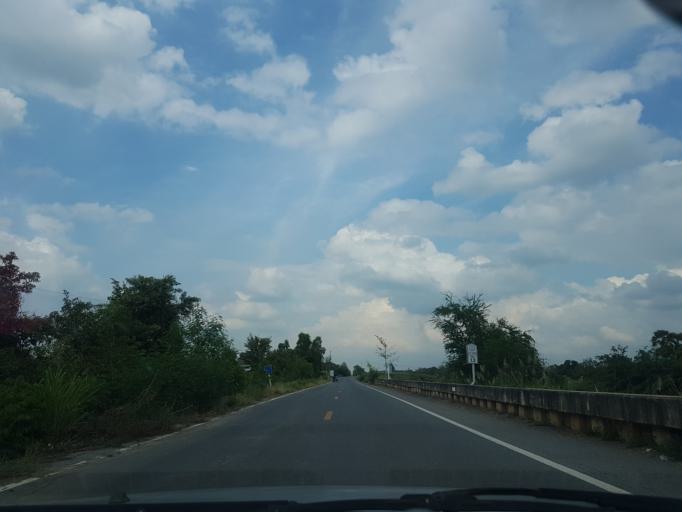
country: TH
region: Pathum Thani
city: Nong Suea
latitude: 14.1940
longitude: 100.8915
